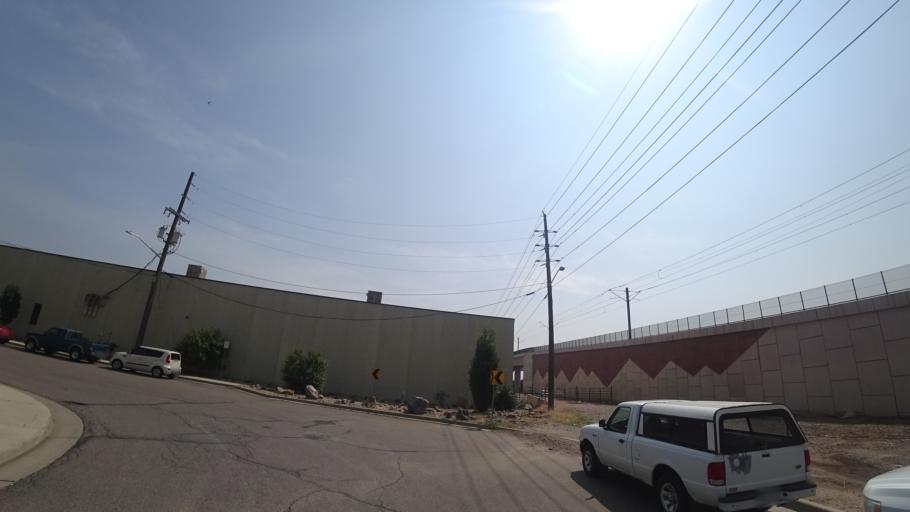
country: US
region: Colorado
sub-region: Arapahoe County
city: Littleton
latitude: 39.6333
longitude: -105.0074
